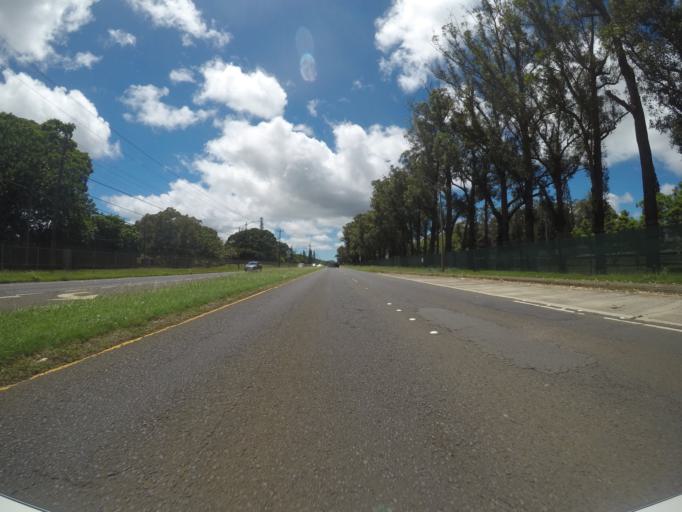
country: US
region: Hawaii
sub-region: Honolulu County
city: Schofield Barracks
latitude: 21.4908
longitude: -158.0453
